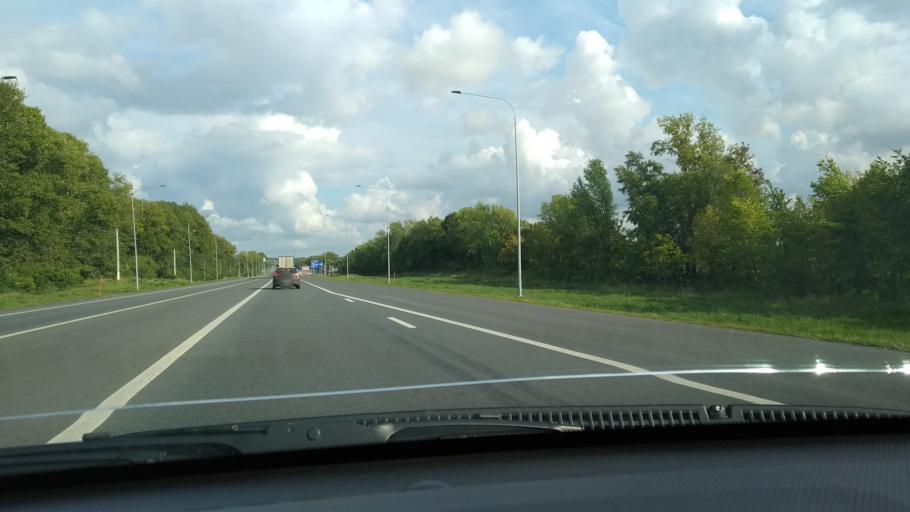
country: RU
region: Tatarstan
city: Stolbishchi
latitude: 55.6586
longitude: 49.3046
